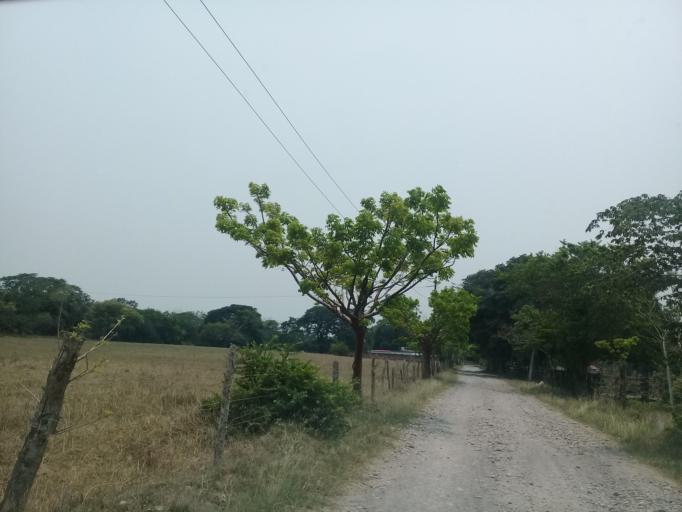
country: MX
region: Veracruz
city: Jamapa
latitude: 18.9324
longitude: -96.2086
